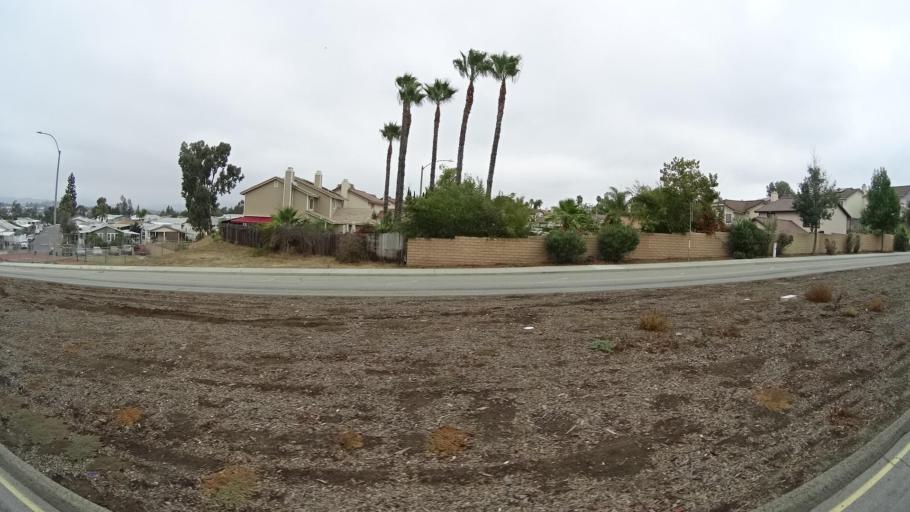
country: US
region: California
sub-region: San Diego County
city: Escondido
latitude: 33.0995
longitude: -117.1129
